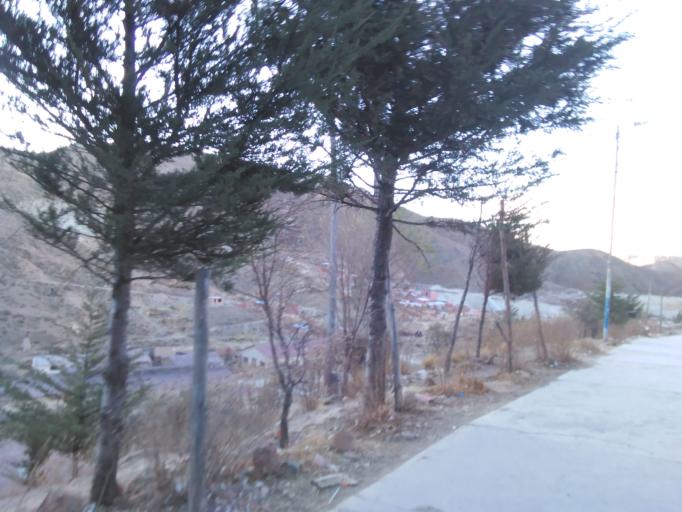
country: BO
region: Potosi
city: Llallagua
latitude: -18.4227
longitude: -66.5912
